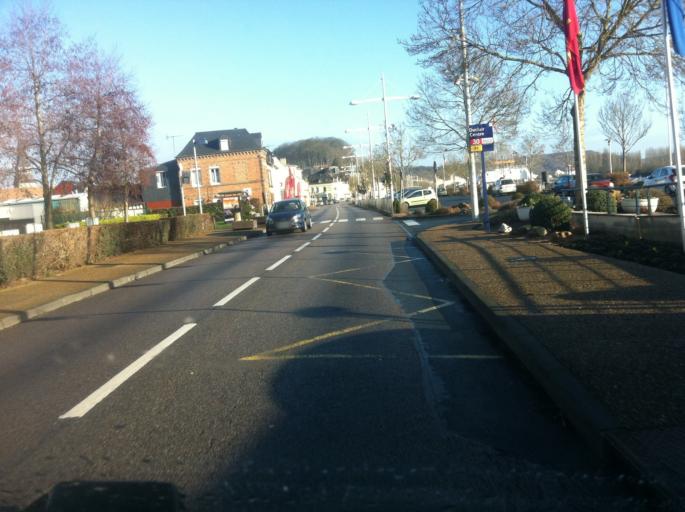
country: FR
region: Haute-Normandie
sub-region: Departement de la Seine-Maritime
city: Duclair
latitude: 49.4797
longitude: 0.8719
